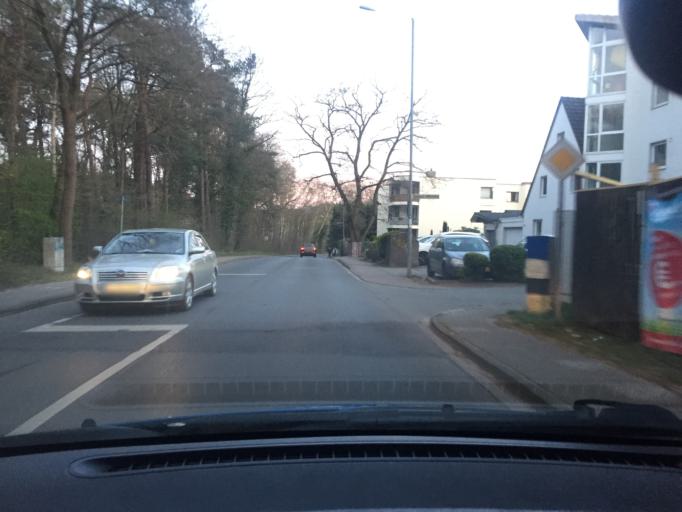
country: DE
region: Lower Saxony
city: Buchholz in der Nordheide
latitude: 53.3221
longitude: 9.8580
